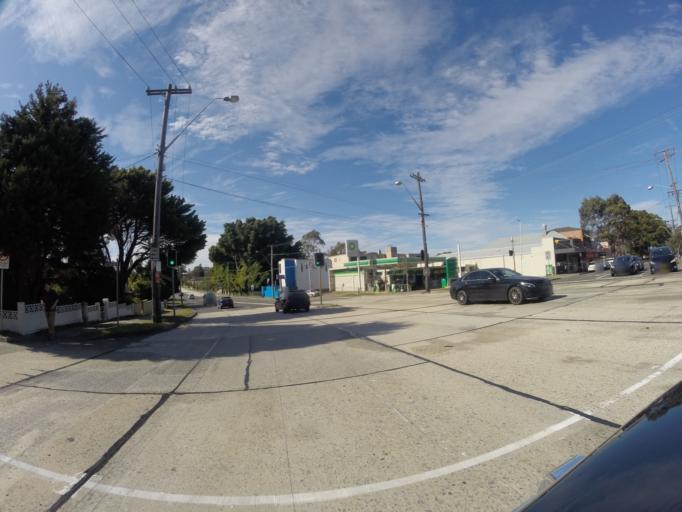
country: AU
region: New South Wales
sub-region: Kogarah
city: Kogarah
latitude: -33.9820
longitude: 151.1172
